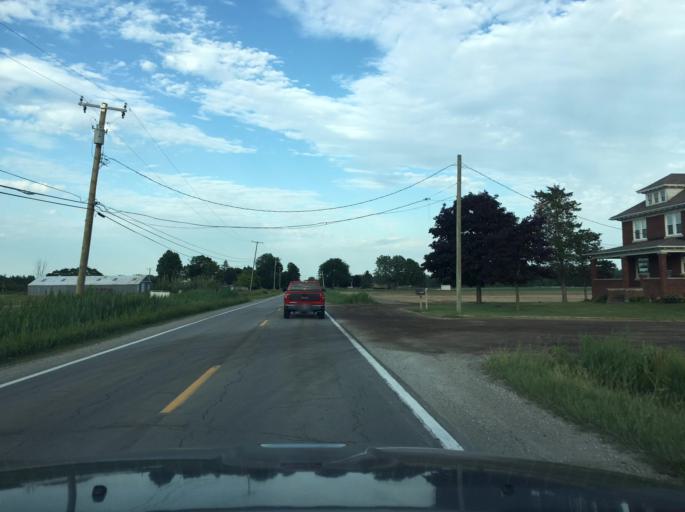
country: US
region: Michigan
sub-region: Macomb County
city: New Haven
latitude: 42.7170
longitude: -82.9180
